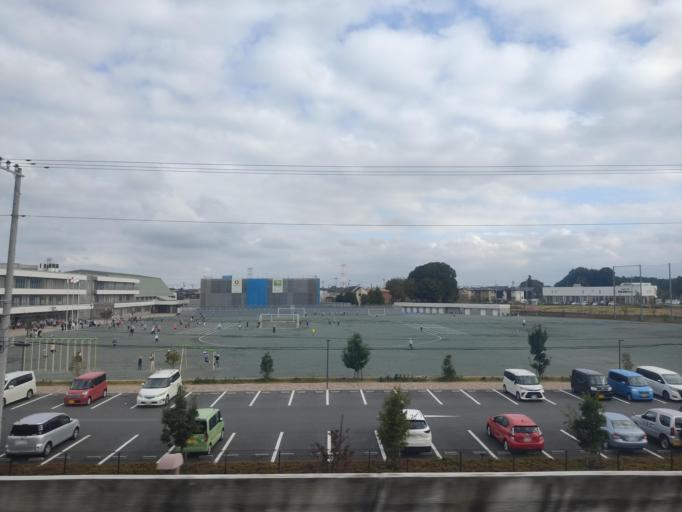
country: JP
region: Ibaraki
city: Mitsukaido
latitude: 36.0261
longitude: 140.0553
